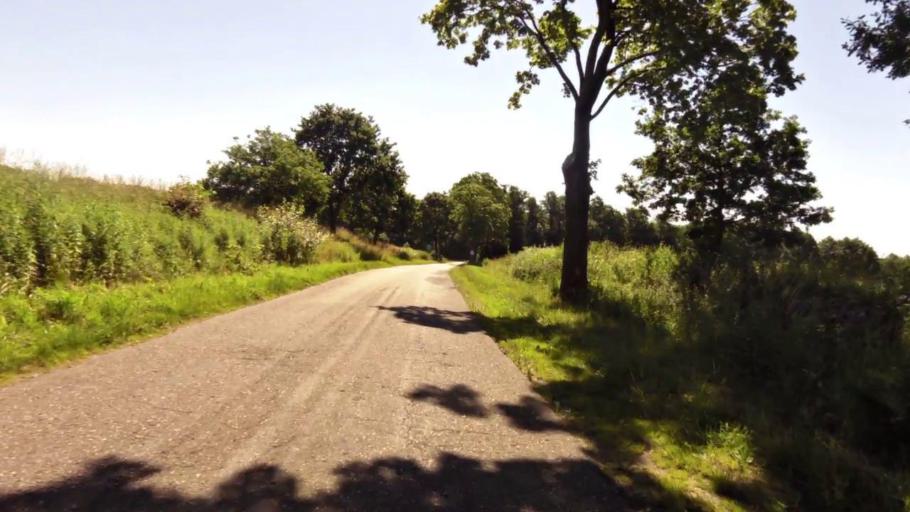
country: PL
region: West Pomeranian Voivodeship
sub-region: Powiat bialogardzki
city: Bialogard
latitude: 53.9369
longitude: 15.9890
